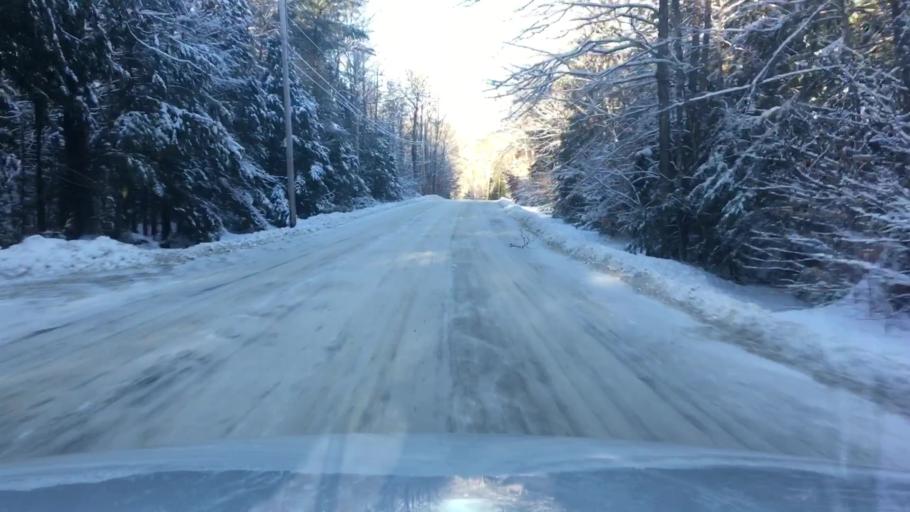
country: US
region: Maine
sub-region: Kennebec County
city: Belgrade
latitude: 44.4257
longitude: -69.8918
